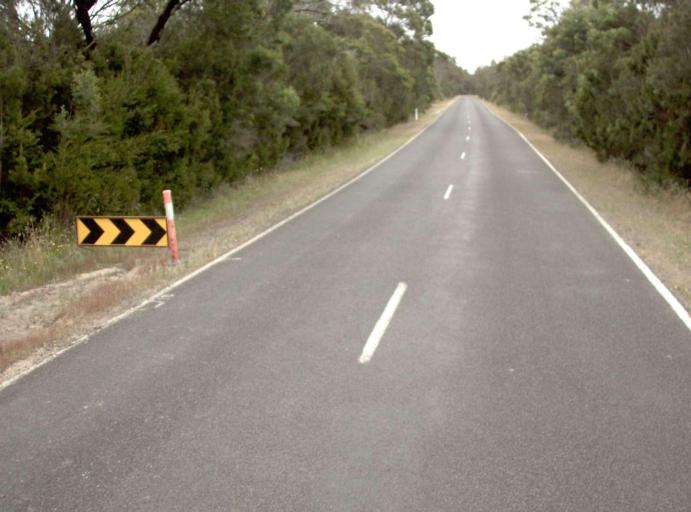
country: AU
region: Victoria
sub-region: Latrobe
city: Traralgon
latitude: -38.5048
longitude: 146.8410
